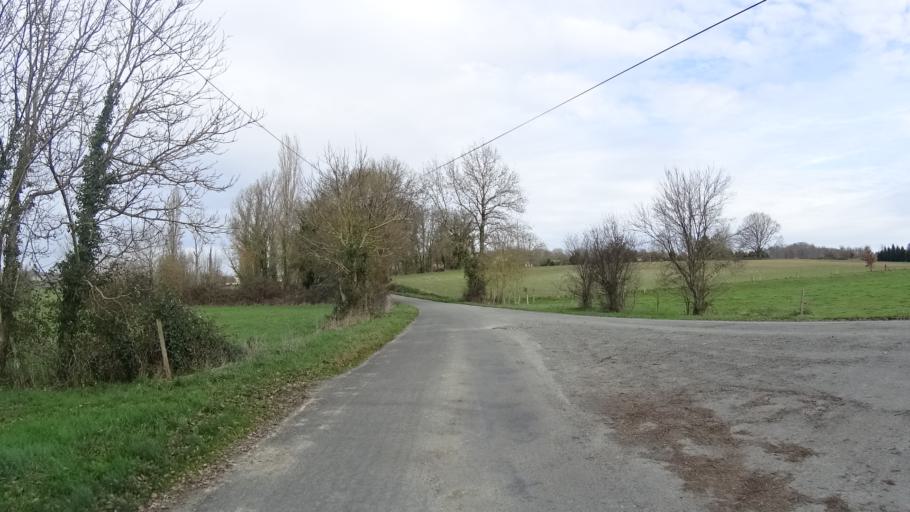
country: FR
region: Aquitaine
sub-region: Departement de la Dordogne
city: Saint-Aulaye
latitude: 45.2301
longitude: 0.1619
